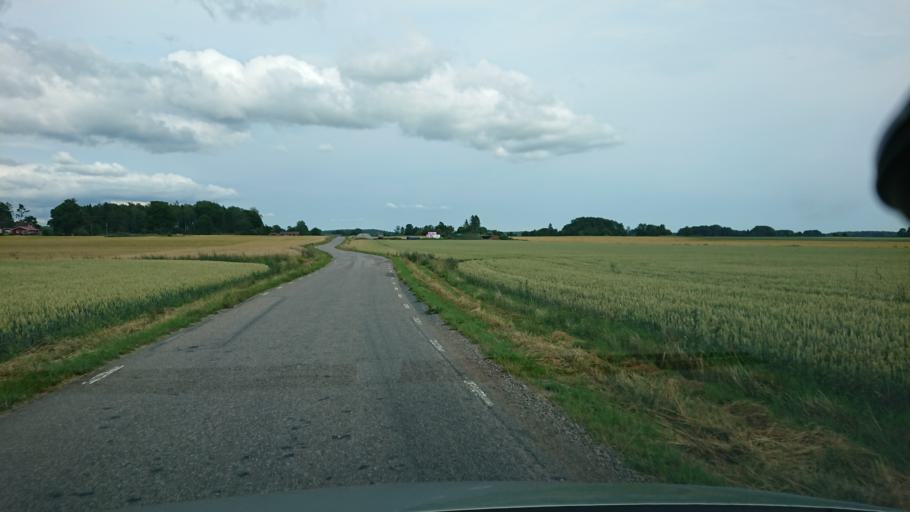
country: SE
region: Uppsala
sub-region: Osthammars Kommun
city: Bjorklinge
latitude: 59.9905
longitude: 17.5164
